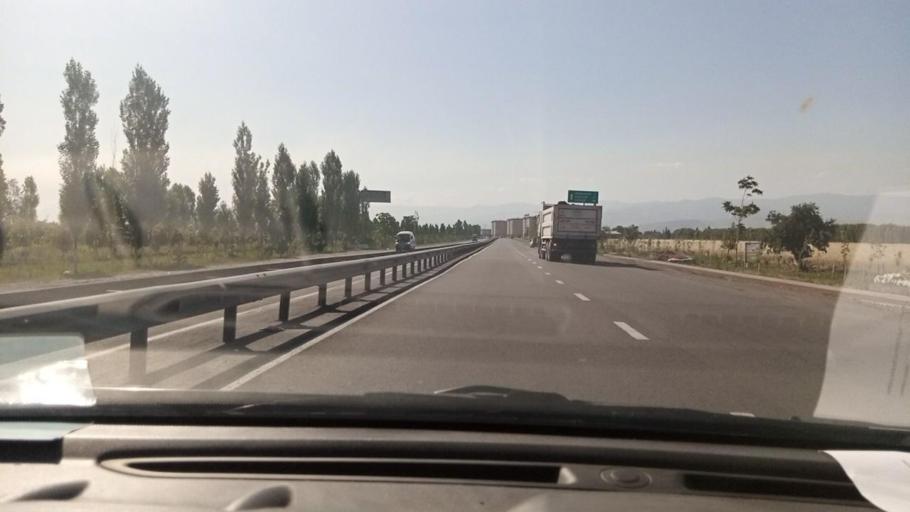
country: UZ
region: Toshkent
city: Ohangaron
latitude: 40.9183
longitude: 69.6013
